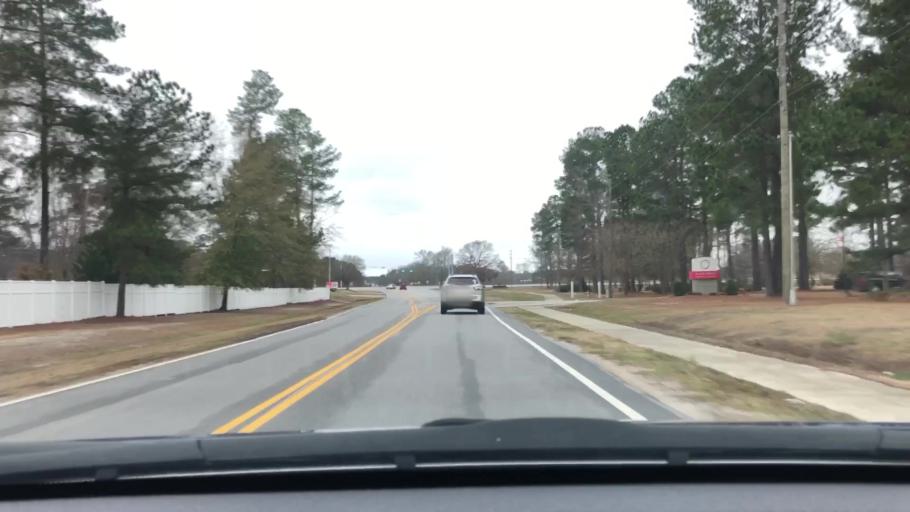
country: US
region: South Carolina
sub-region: Sumter County
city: Cherryvale
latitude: 33.9369
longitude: -80.4172
